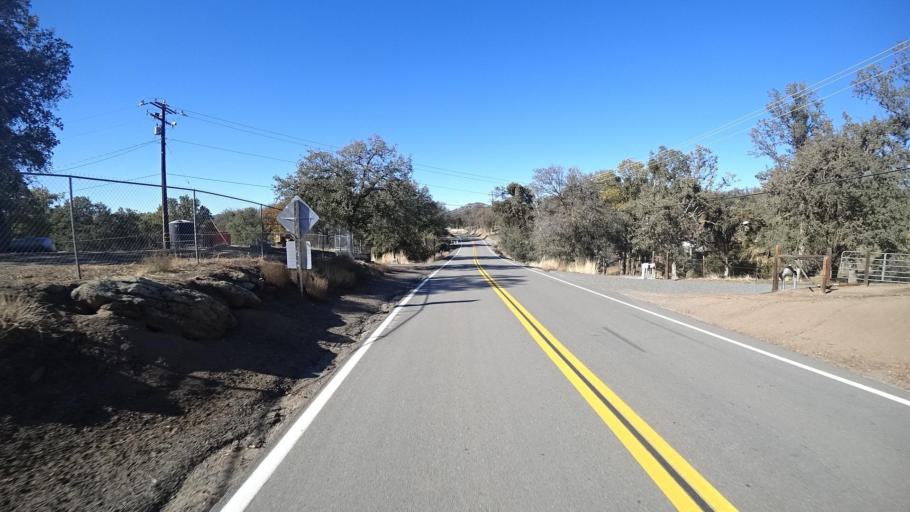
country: US
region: California
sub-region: Kern County
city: Alta Sierra
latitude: 35.7289
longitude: -118.7055
